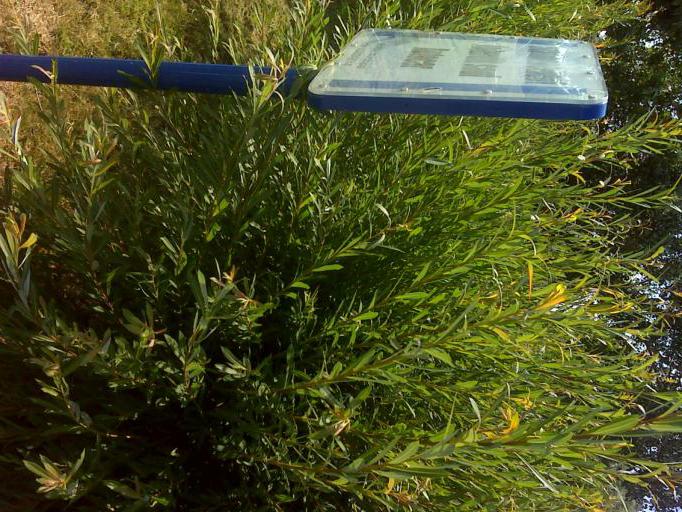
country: FR
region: Champagne-Ardenne
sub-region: Departement de la Haute-Marne
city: Montier-en-Der
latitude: 48.5535
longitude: 4.7801
